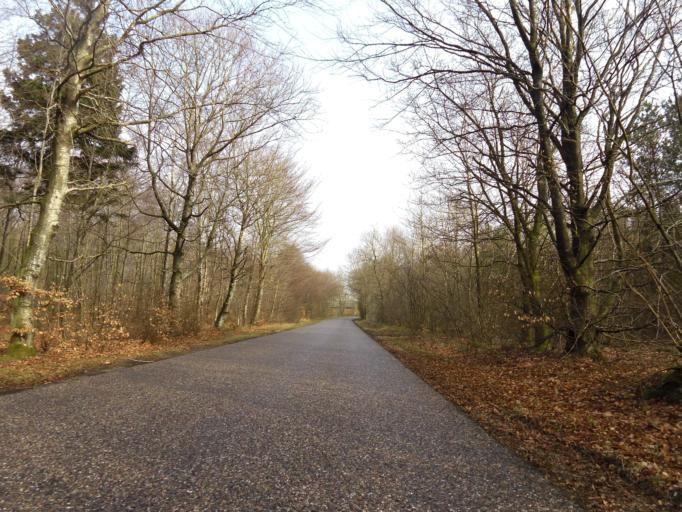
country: DK
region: Central Jutland
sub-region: Holstebro Kommune
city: Vinderup
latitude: 56.4246
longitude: 8.8097
